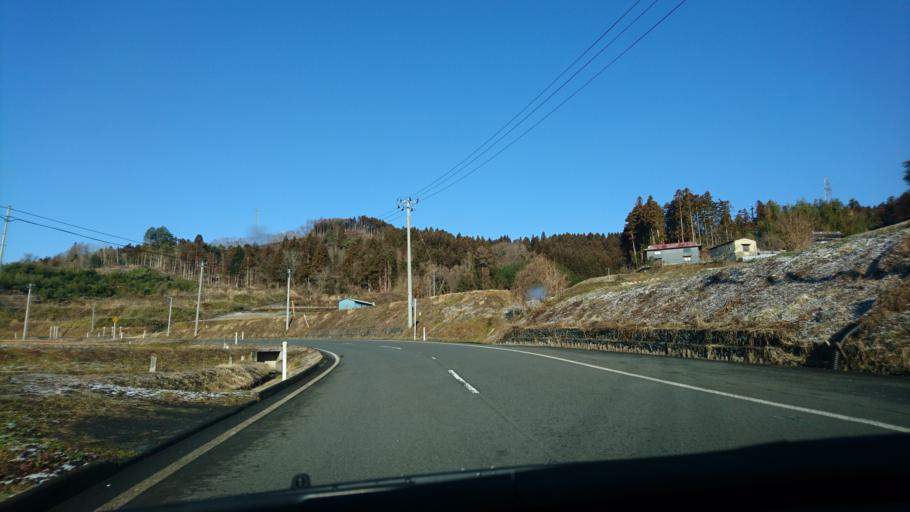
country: JP
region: Iwate
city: Ichinoseki
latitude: 38.8800
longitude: 141.3174
